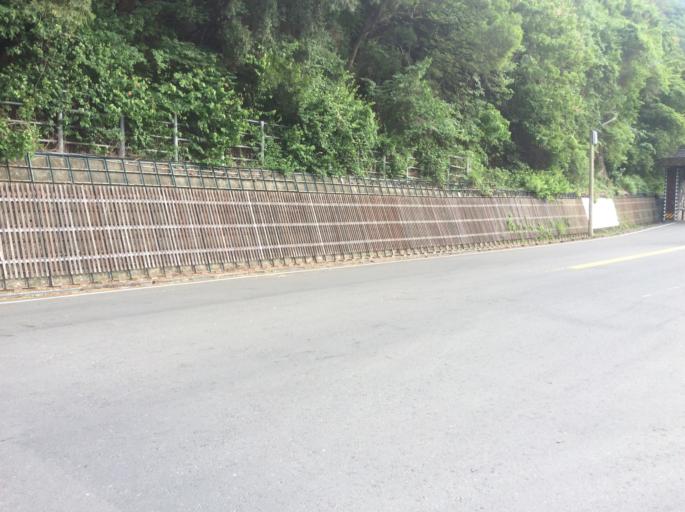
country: TW
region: Taiwan
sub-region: Pingtung
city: Pingtung
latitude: 22.8803
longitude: 120.6498
